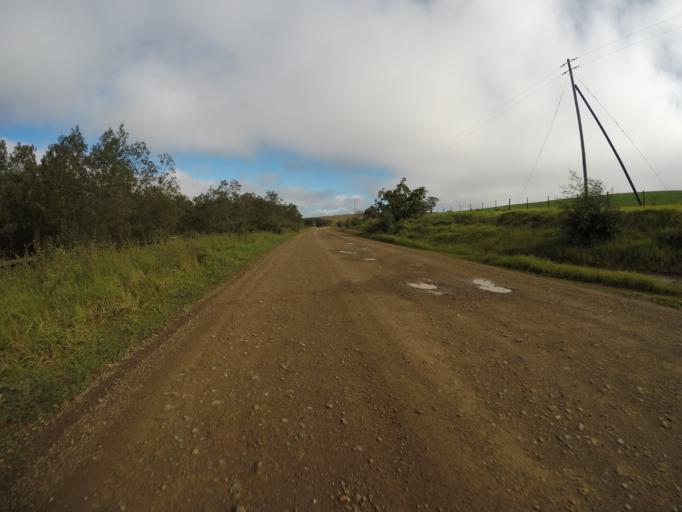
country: ZA
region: Western Cape
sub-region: Cape Winelands District Municipality
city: Ashton
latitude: -34.1122
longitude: 19.7948
